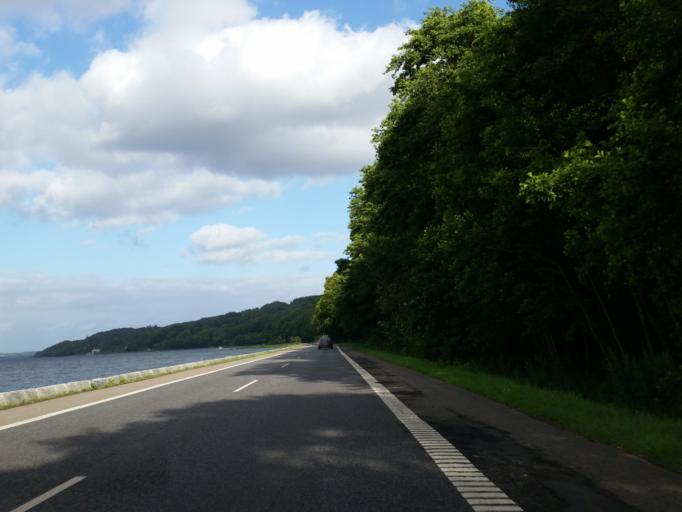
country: DK
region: South Denmark
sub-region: Vejle Kommune
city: Vejle
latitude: 55.6921
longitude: 9.5749
